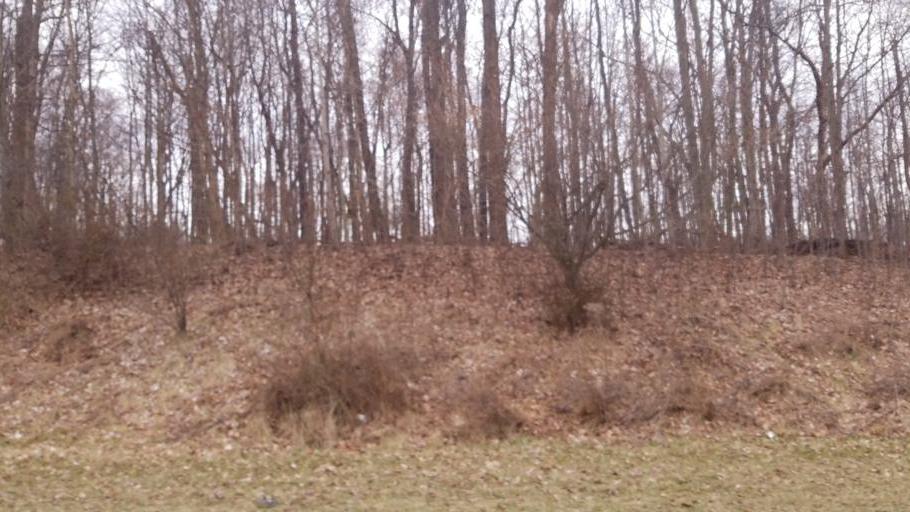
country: US
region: Ohio
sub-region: Richland County
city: Mansfield
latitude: 40.7334
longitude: -82.4947
